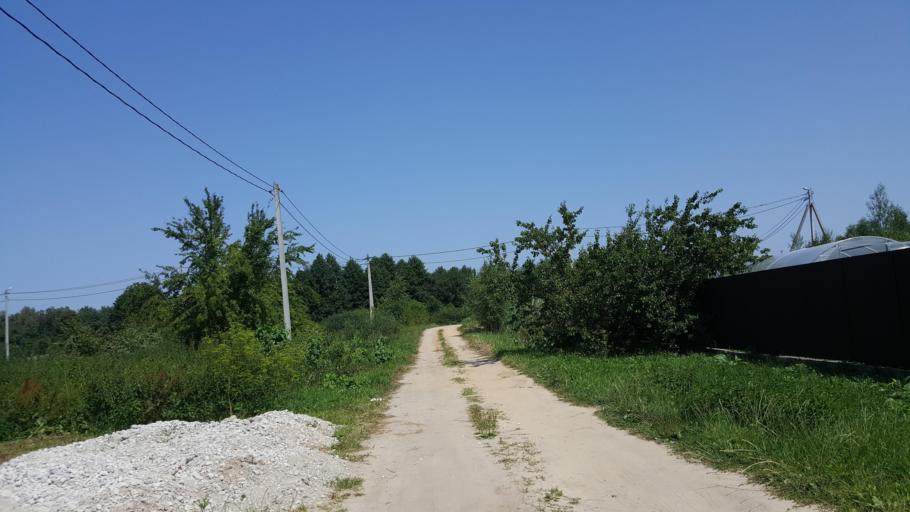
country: BY
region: Brest
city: Zhabinka
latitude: 52.1990
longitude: 23.9935
